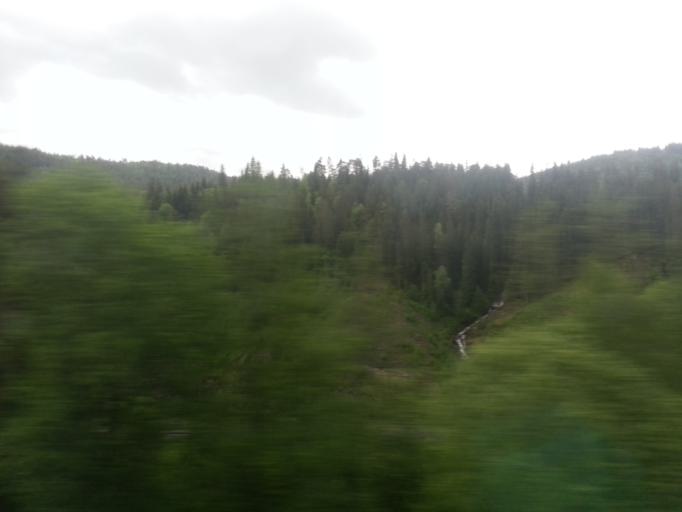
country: NO
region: Sor-Trondelag
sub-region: Midtre Gauldal
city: Storen
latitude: 62.9296
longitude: 10.1746
